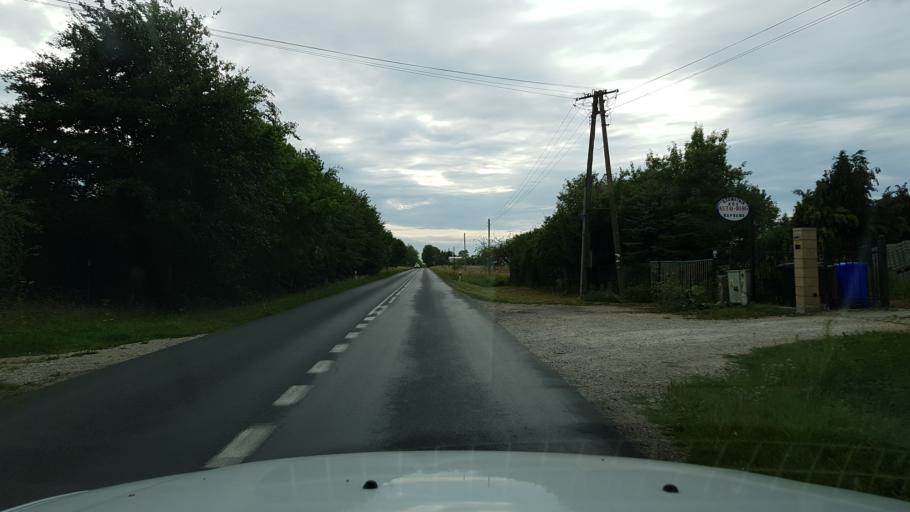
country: PL
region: West Pomeranian Voivodeship
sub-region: Powiat kolobrzeski
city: Dygowo
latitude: 54.1408
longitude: 15.6994
